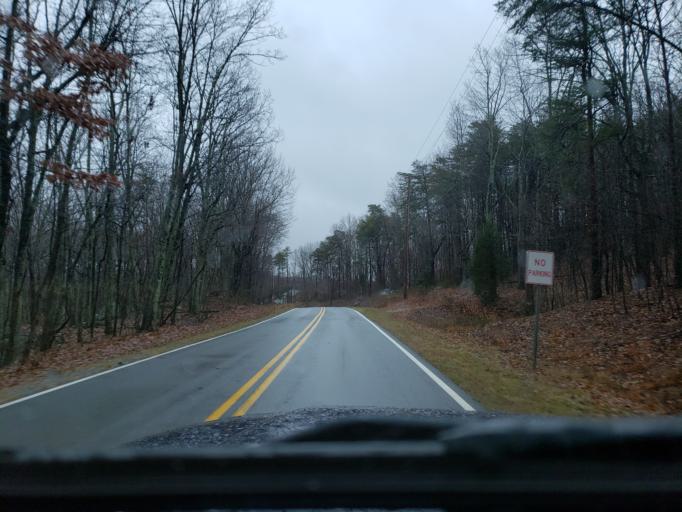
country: US
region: North Carolina
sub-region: Cleveland County
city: White Plains
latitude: 35.1738
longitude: -81.3626
